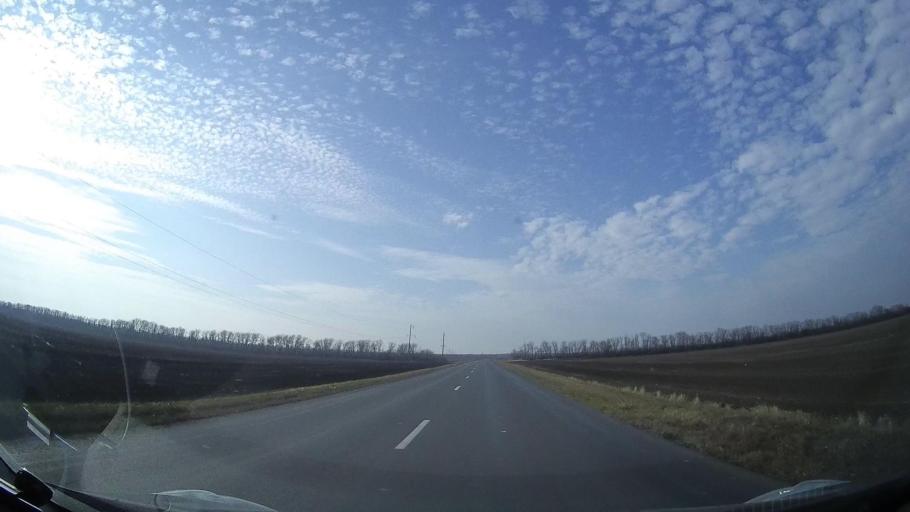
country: RU
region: Rostov
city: Veselyy
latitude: 46.9694
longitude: 40.6486
